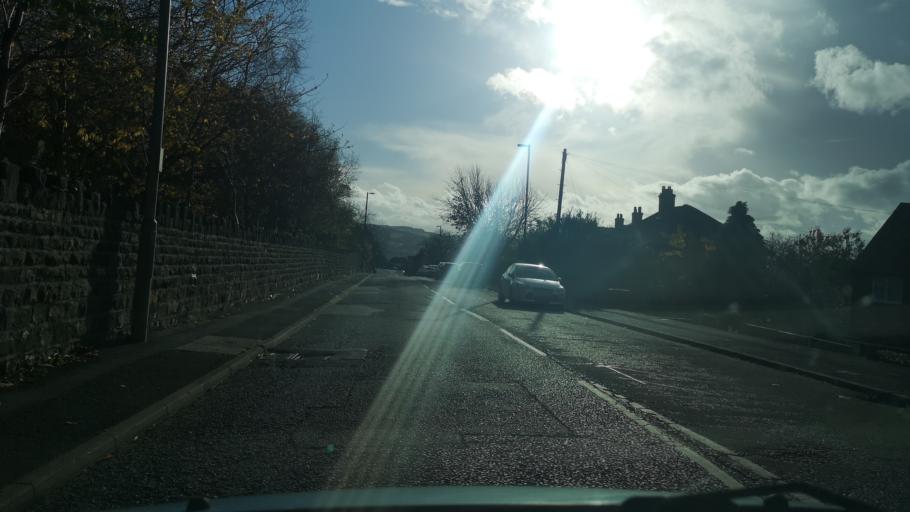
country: GB
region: England
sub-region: Kirklees
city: Batley
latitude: 53.6930
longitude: -1.6523
